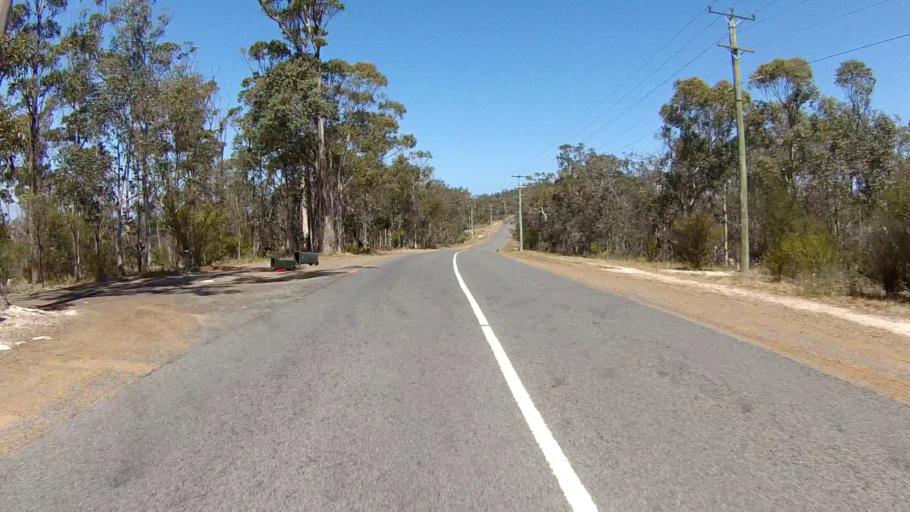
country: AU
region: Tasmania
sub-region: Clarence
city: Sandford
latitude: -43.0048
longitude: 147.4787
